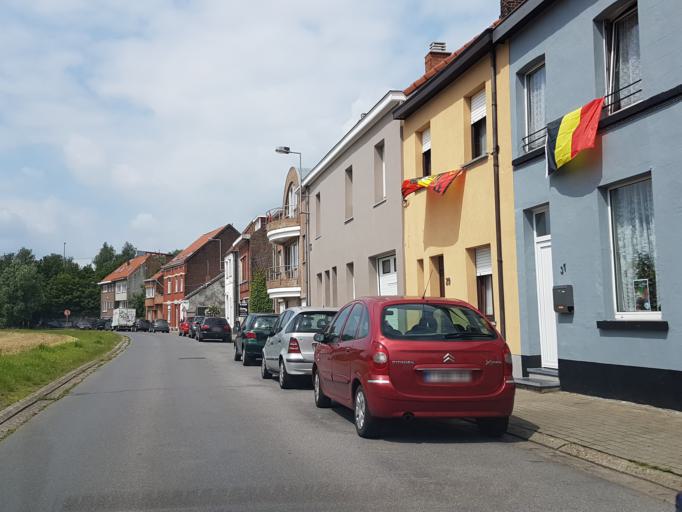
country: BE
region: Flanders
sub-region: Provincie Vlaams-Brabant
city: Diegem
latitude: 50.8926
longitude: 4.4452
